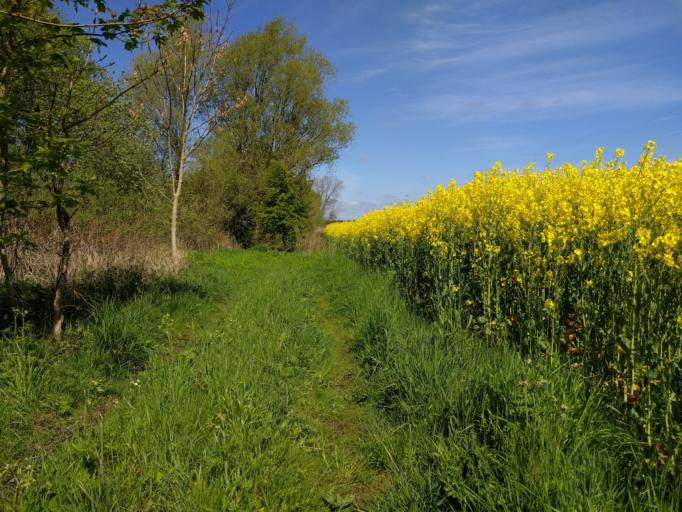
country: DK
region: South Denmark
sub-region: Kerteminde Kommune
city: Langeskov
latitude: 55.3879
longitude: 10.5628
